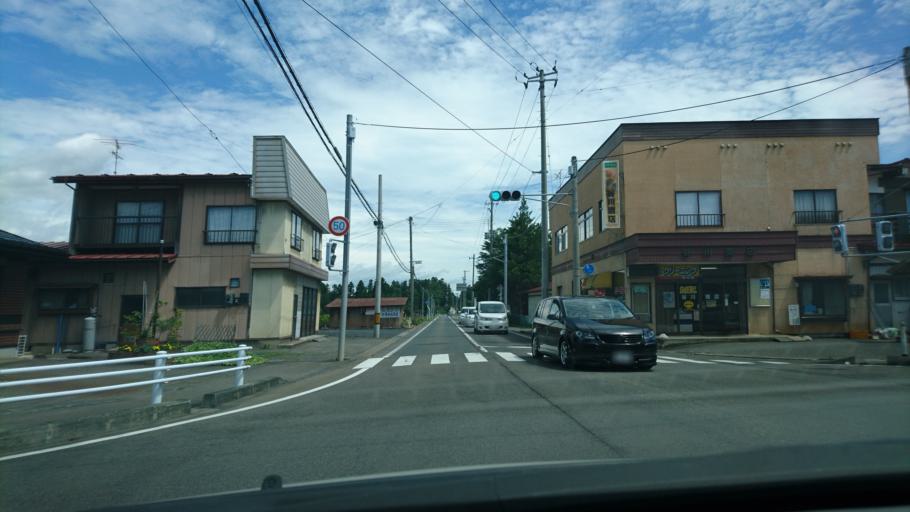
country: JP
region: Iwate
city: Hanamaki
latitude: 39.4055
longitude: 141.1676
